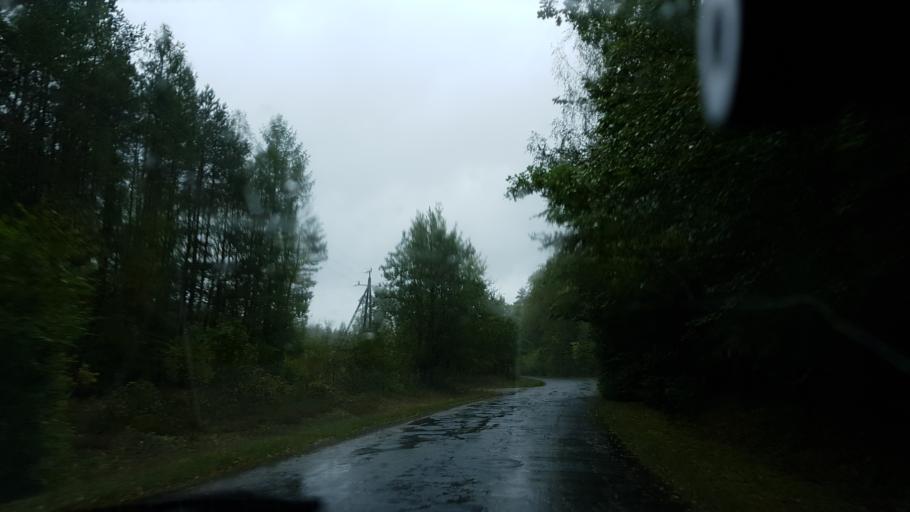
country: PL
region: West Pomeranian Voivodeship
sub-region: Powiat goleniowski
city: Przybiernow
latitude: 53.6718
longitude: 14.7336
